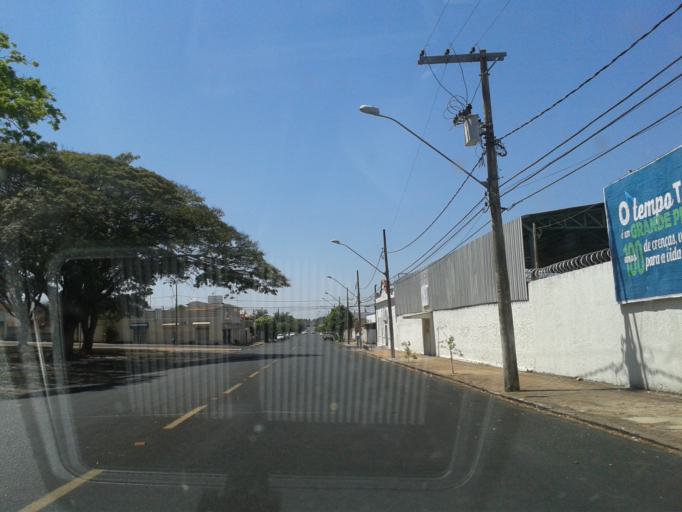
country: BR
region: Minas Gerais
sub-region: Araguari
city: Araguari
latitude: -18.6431
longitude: -48.1922
